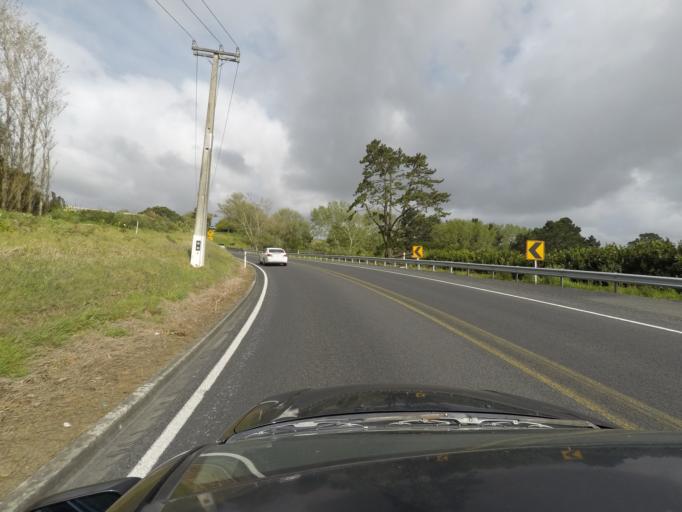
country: NZ
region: Auckland
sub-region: Auckland
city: Pakuranga
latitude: -36.9296
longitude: 174.9363
